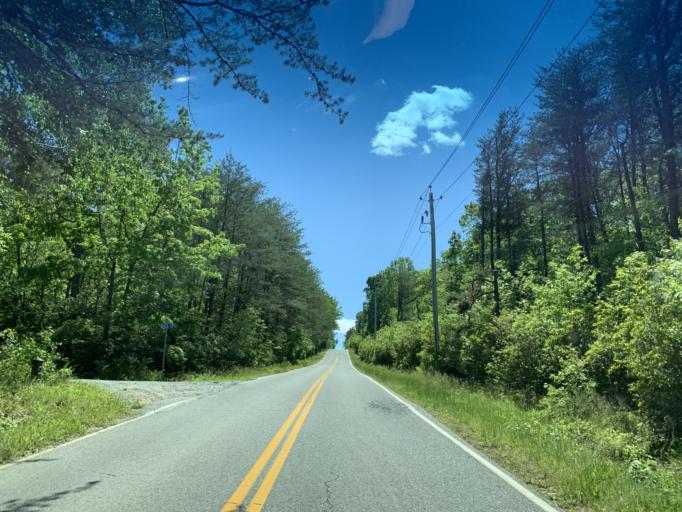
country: US
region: Maryland
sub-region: Cecil County
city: Charlestown
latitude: 39.5335
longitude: -75.9313
